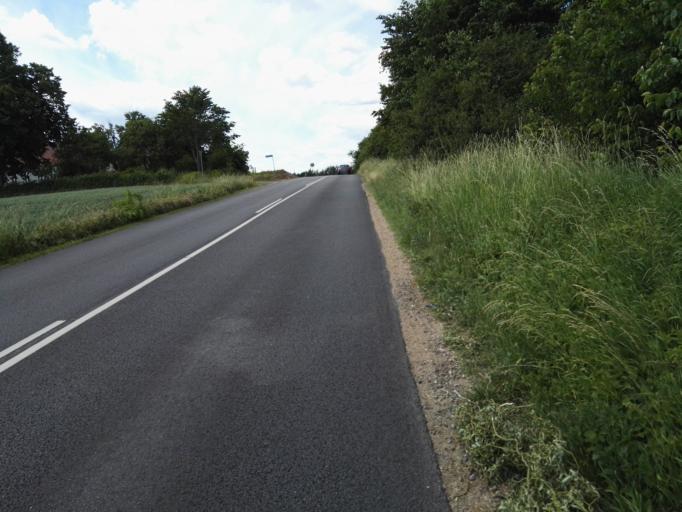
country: DK
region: Capital Region
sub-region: Egedal Kommune
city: Olstykke
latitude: 55.7666
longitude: 12.1602
